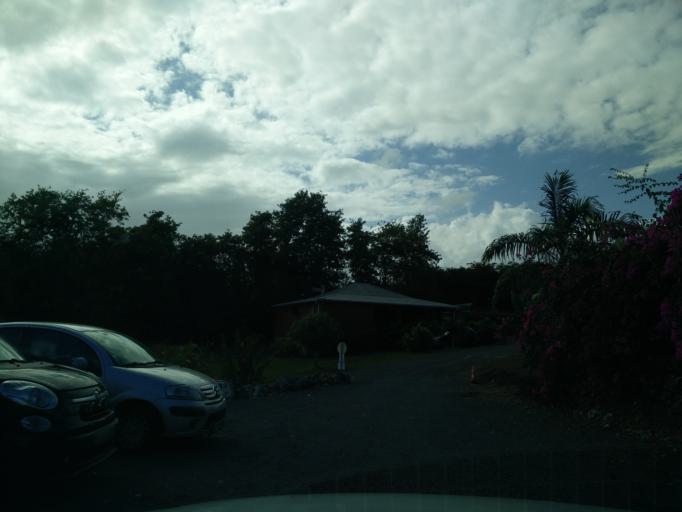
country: GP
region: Guadeloupe
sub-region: Guadeloupe
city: Sainte-Anne
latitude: 16.2478
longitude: -61.3769
